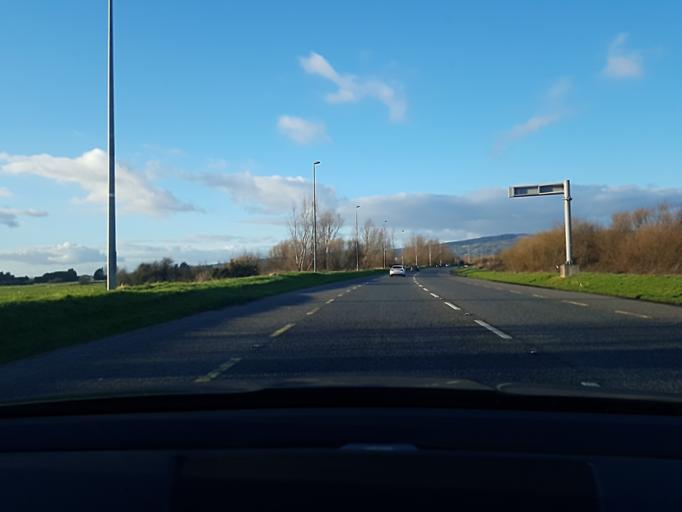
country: IE
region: Munster
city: Moyross
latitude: 52.6671
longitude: -8.6726
